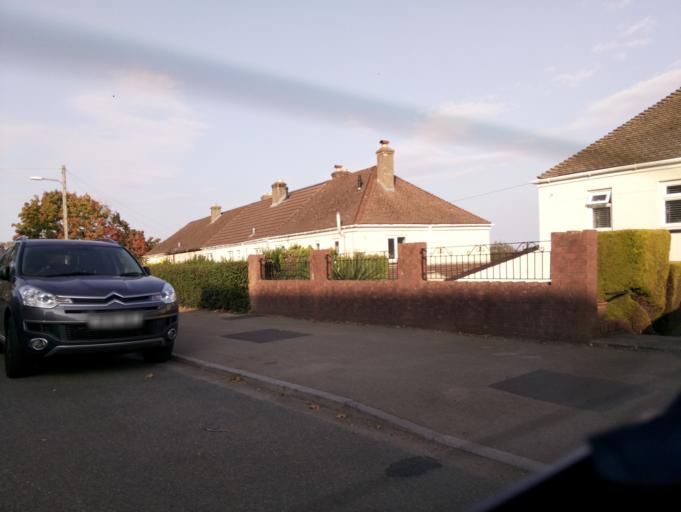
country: GB
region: Wales
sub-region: Torfaen County Borough
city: Pontypool
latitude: 51.6952
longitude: -3.0370
